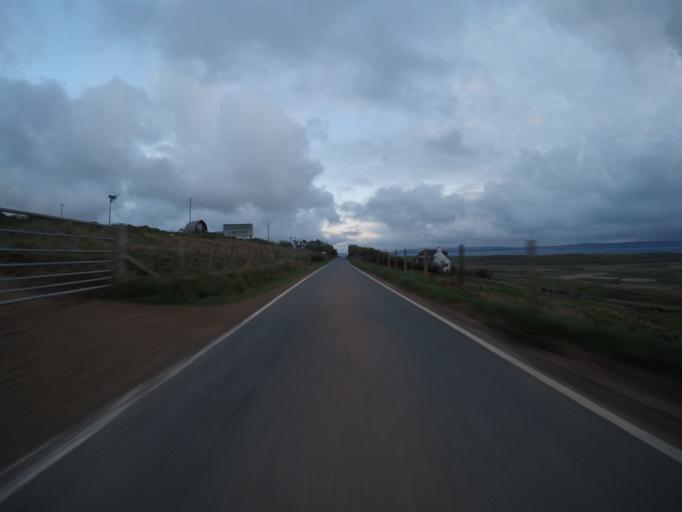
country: GB
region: Scotland
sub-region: Highland
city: Portree
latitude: 57.6338
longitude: -6.3769
